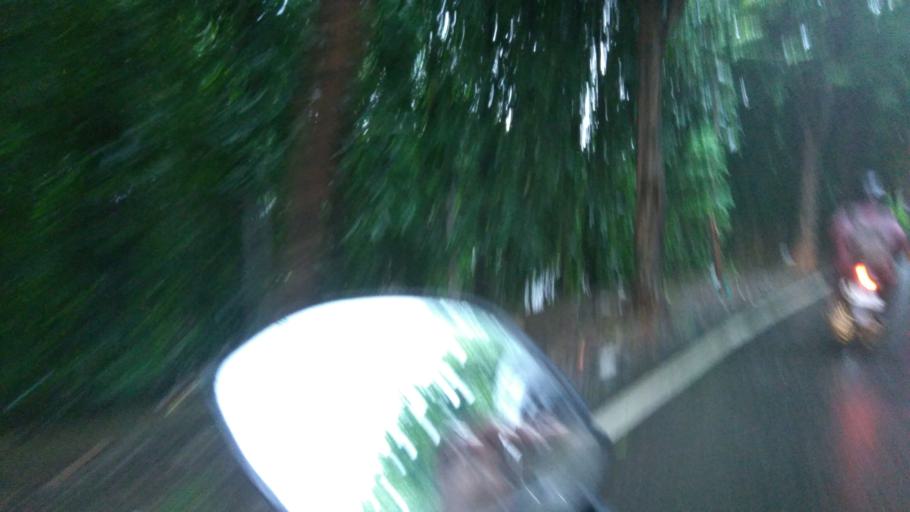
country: ID
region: Central Java
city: Semarang
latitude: -7.0092
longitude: 110.3854
